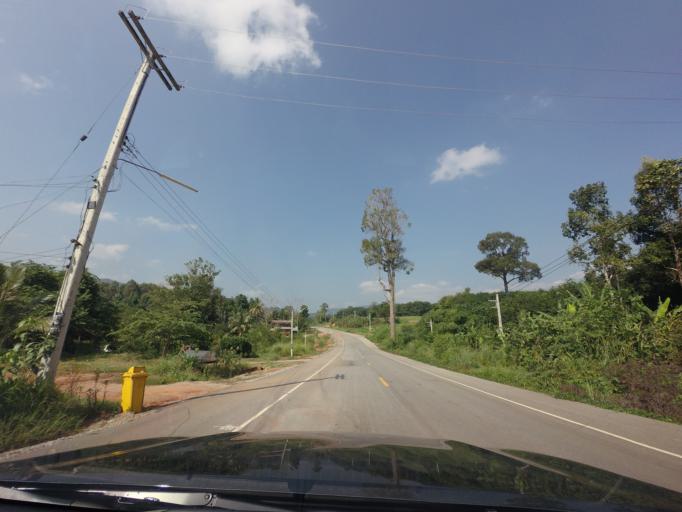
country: TH
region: Loei
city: Na Haeo
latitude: 17.4972
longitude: 101.0345
